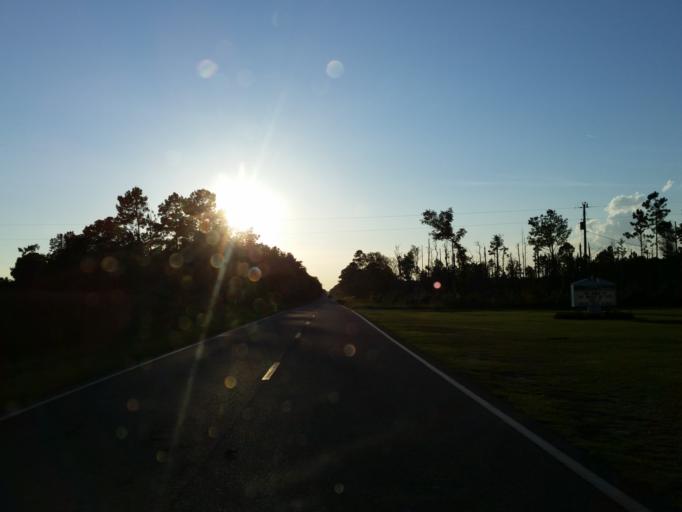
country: US
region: Georgia
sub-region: Lanier County
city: Lakeland
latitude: 31.1660
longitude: -83.0944
